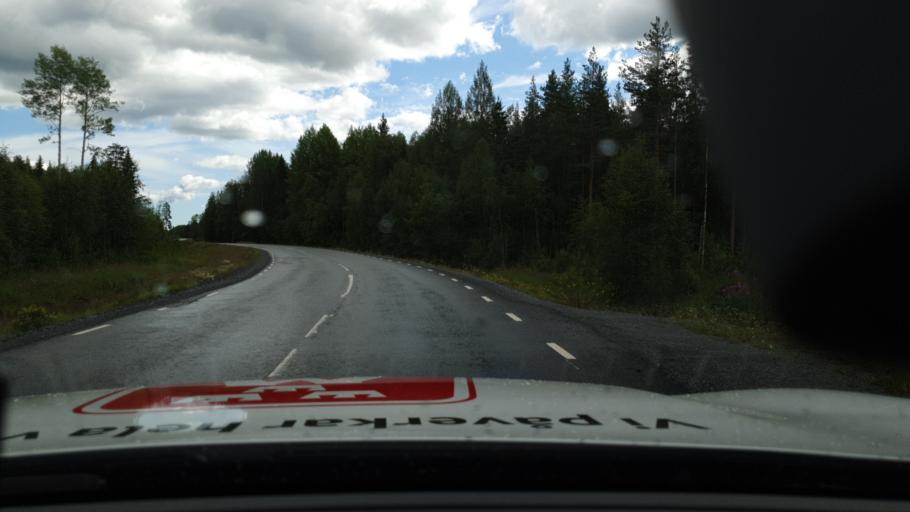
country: SE
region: Norrbotten
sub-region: Bodens Kommun
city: Saevast
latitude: 65.8417
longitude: 21.8039
